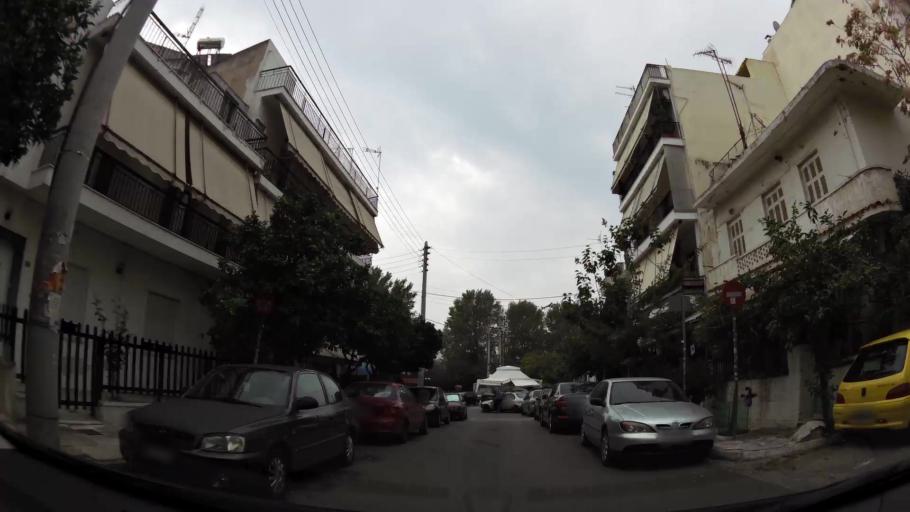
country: GR
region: Attica
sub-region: Nomos Piraios
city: Korydallos
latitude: 37.9794
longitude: 23.6355
